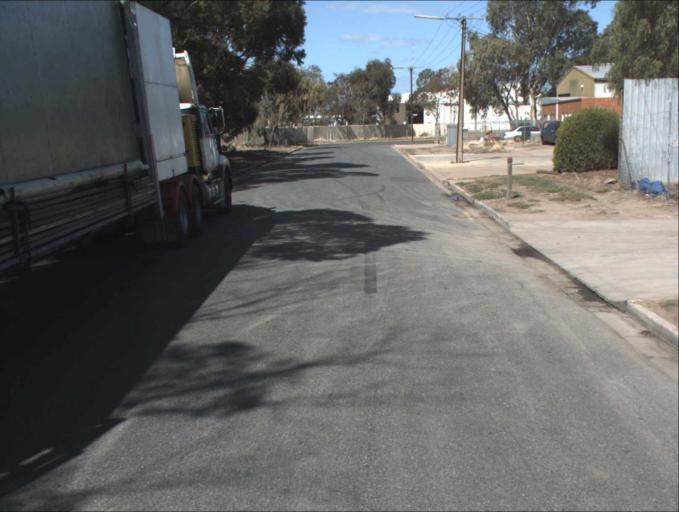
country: AU
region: South Australia
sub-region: Charles Sturt
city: Woodville North
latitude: -34.8370
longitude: 138.5552
